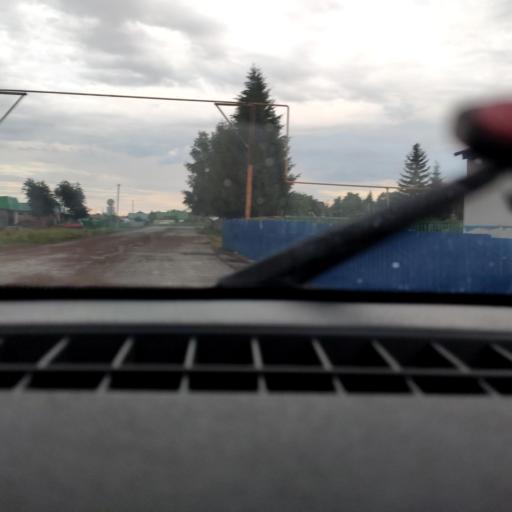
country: RU
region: Bashkortostan
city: Blagoveshchensk
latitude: 54.9313
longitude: 55.9699
